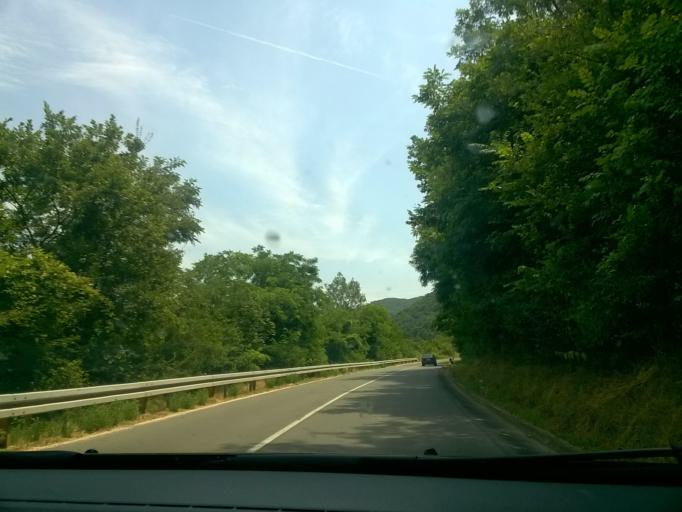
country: RS
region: Central Serbia
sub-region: Nisavski Okrug
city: Aleksinac
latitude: 43.6508
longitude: 21.7299
